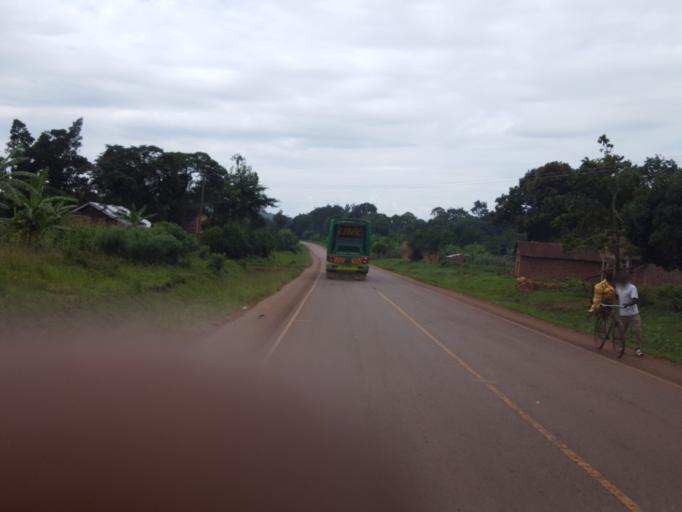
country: UG
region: Central Region
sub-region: Mityana District
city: Mityana
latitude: 0.6683
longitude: 32.0867
